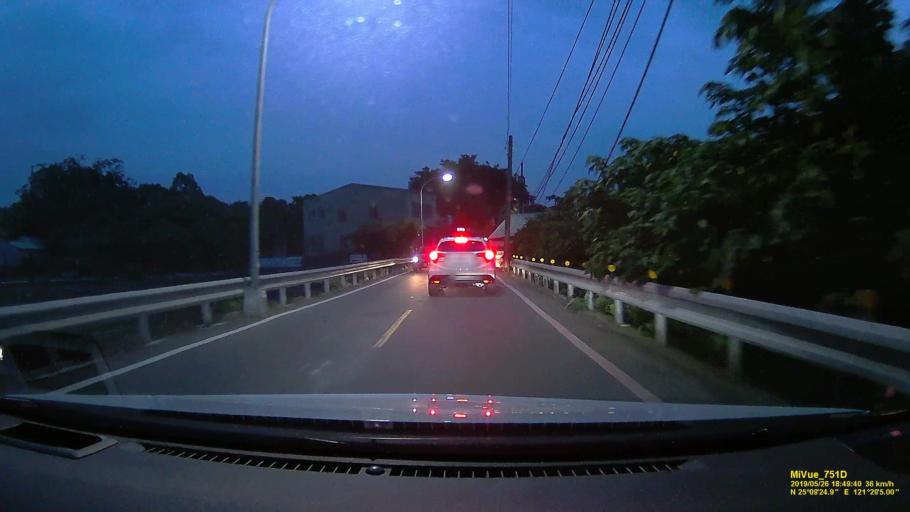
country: TW
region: Taipei
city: Taipei
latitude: 25.1565
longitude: 121.4849
